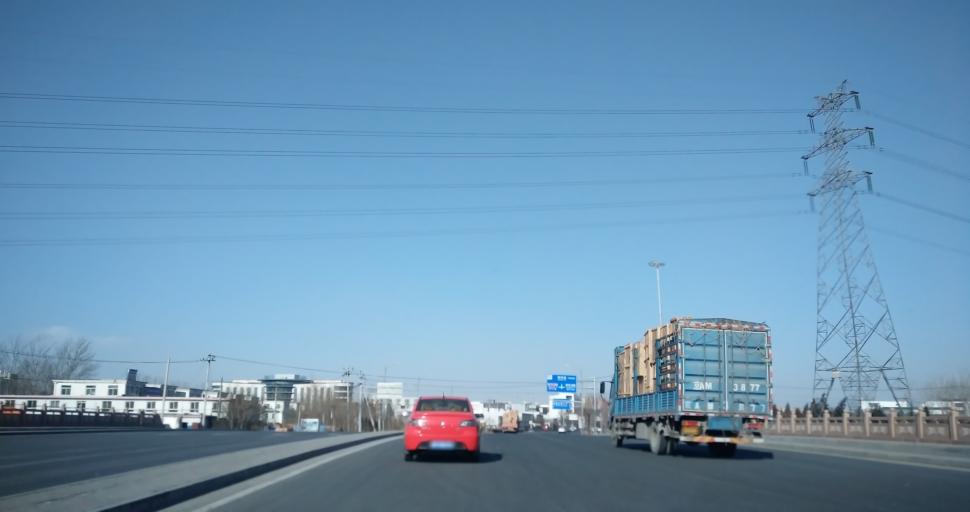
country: CN
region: Beijing
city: Qingyundian
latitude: 39.7364
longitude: 116.4956
